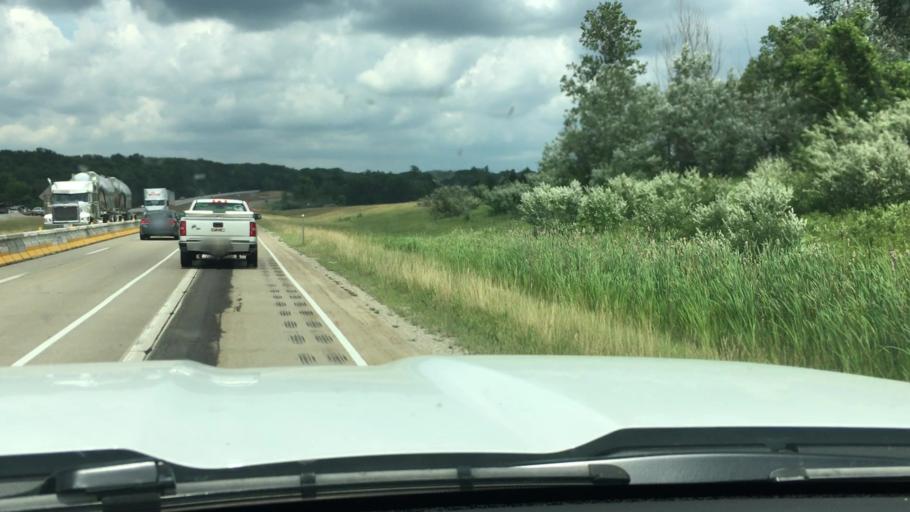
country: US
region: Michigan
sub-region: Kent County
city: Rockford
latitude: 43.1180
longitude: -85.6060
